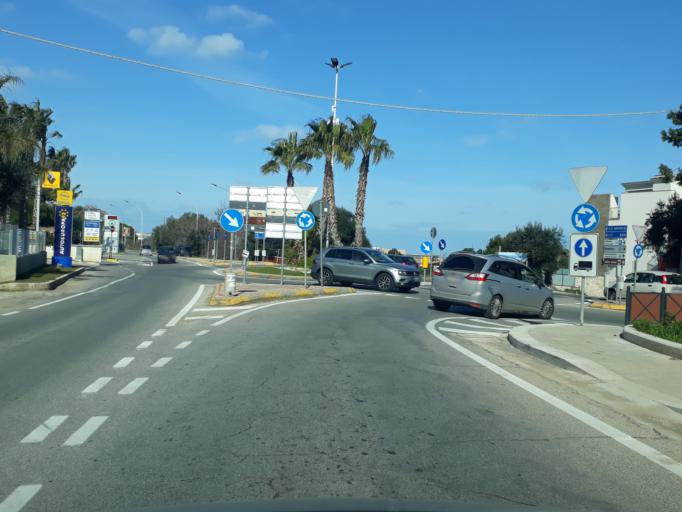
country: IT
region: Apulia
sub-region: Provincia di Bari
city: Monopoli
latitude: 40.9616
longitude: 17.2810
